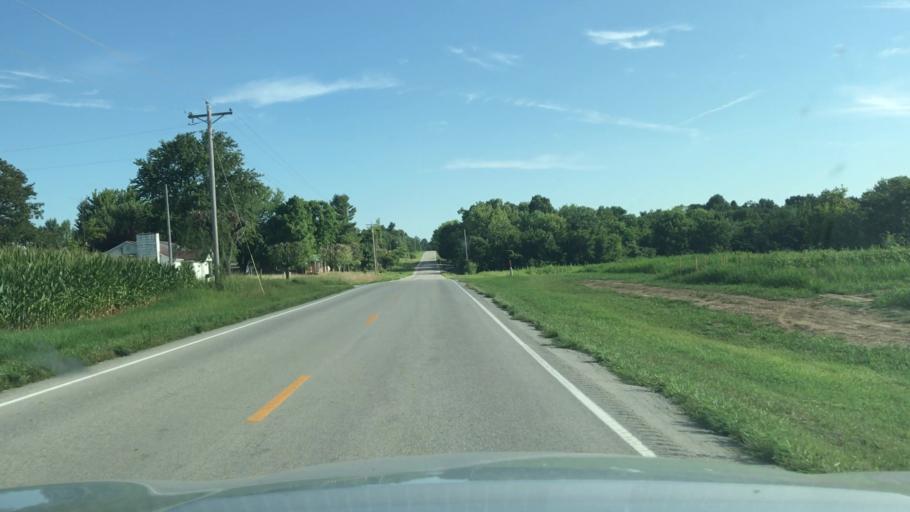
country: US
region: Kentucky
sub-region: Todd County
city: Elkton
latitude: 36.9236
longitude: -87.1625
